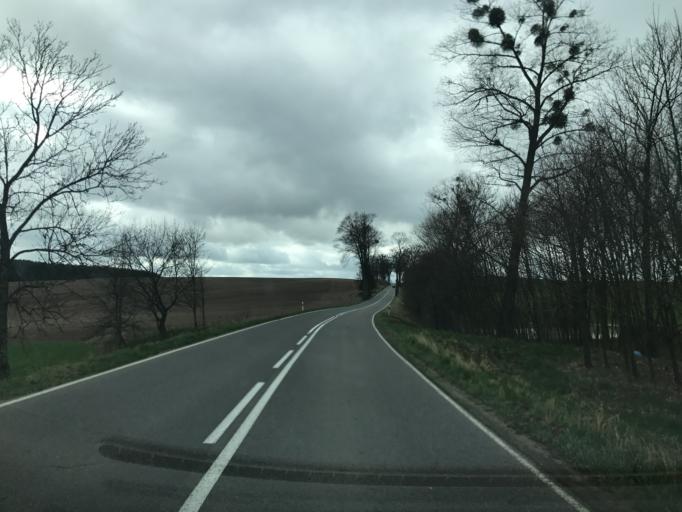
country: PL
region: Warmian-Masurian Voivodeship
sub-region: Powiat ostrodzki
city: Gierzwald
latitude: 53.4972
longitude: 20.1560
